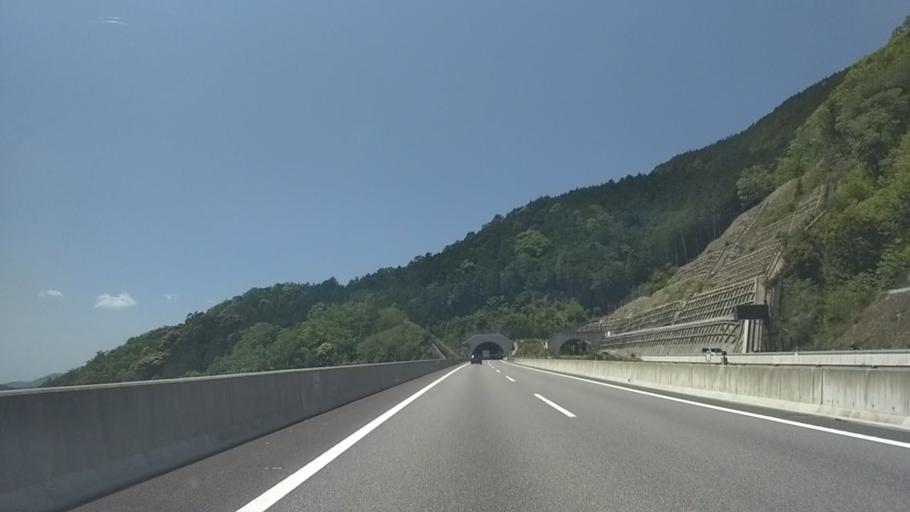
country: JP
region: Aichi
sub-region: Tokai-shi
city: Toyokawa
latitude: 34.8822
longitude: 137.3841
